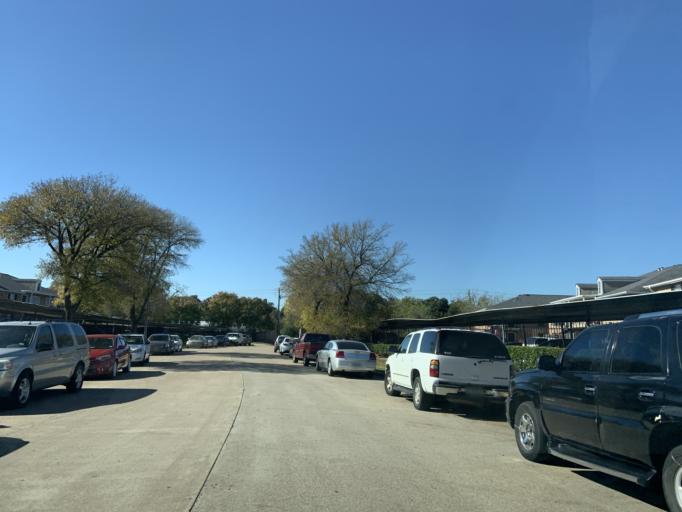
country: US
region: Texas
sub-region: Harris County
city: Bellaire
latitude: 29.6825
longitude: -95.5094
